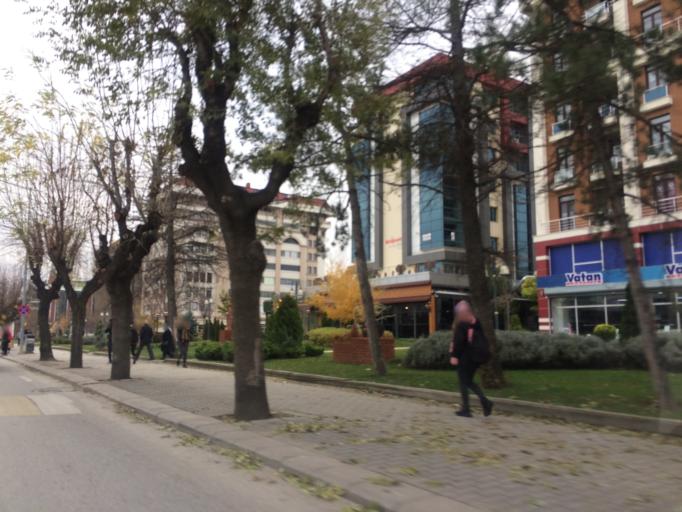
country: TR
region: Eskisehir
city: Eskisehir
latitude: 39.7846
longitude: 30.5024
